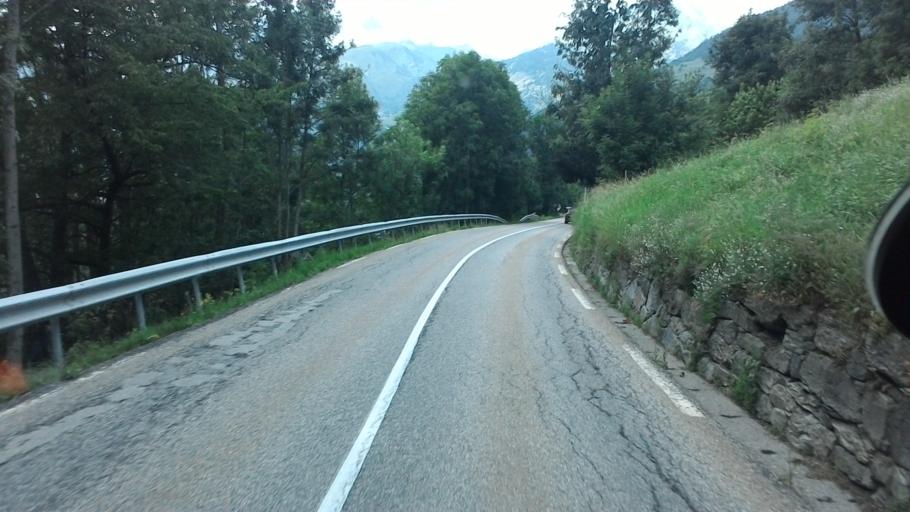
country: FR
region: Rhone-Alpes
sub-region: Departement de la Savoie
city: Seez
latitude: 45.6192
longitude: 6.8224
